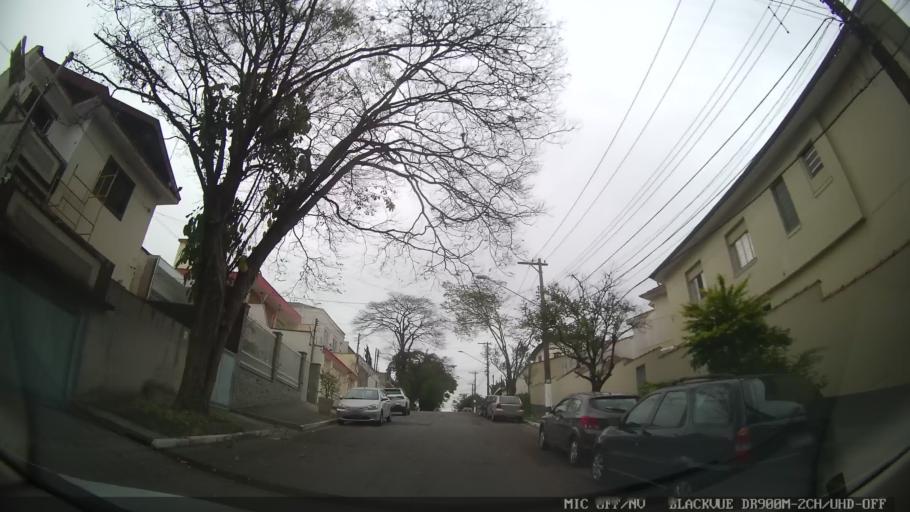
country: BR
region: Sao Paulo
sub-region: Sao Paulo
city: Sao Paulo
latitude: -23.5837
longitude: -46.6200
